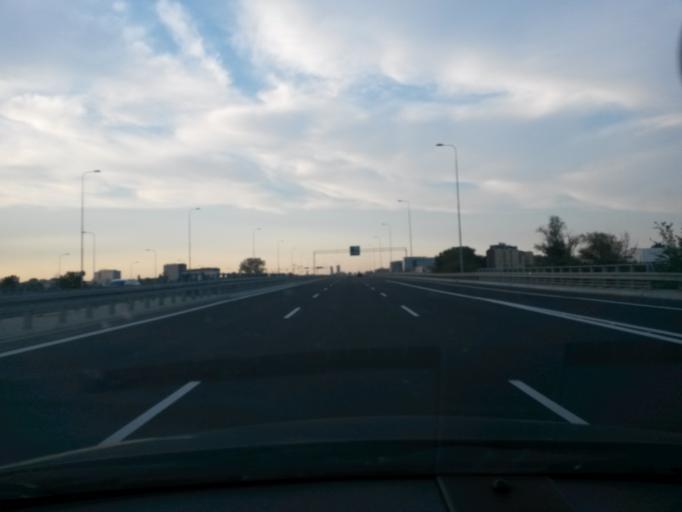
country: PL
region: Masovian Voivodeship
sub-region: Warszawa
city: Wlochy
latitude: 52.1707
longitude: 20.9862
